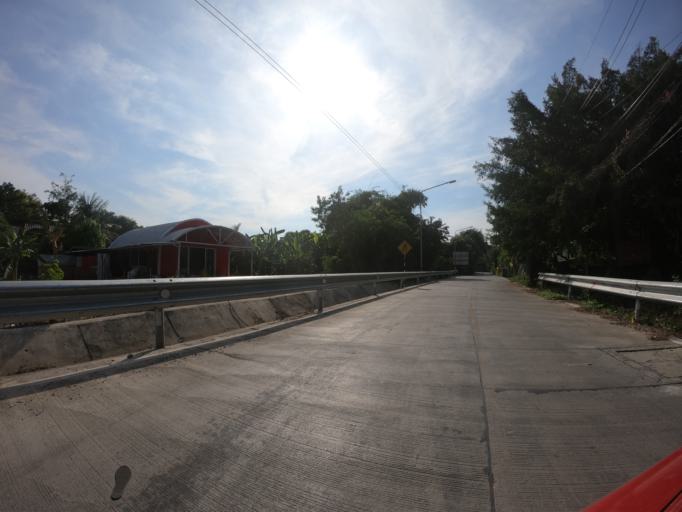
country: TH
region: Pathum Thani
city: Thanyaburi
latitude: 14.0177
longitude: 100.7333
